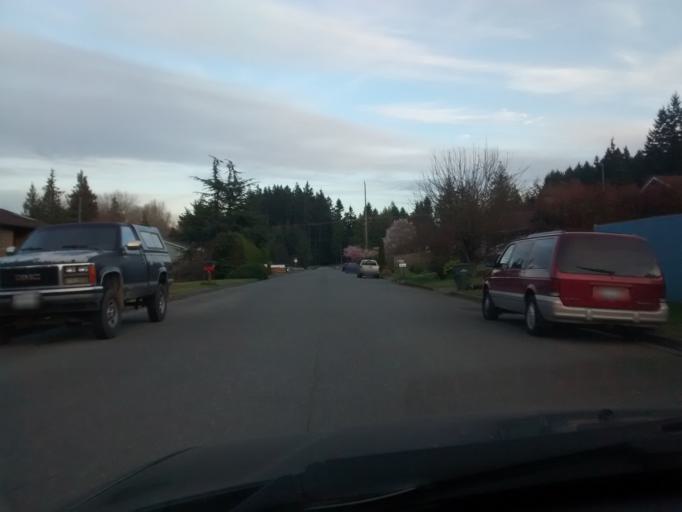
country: US
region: Washington
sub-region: Clallam County
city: Port Angeles
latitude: 48.1198
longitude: -123.4763
